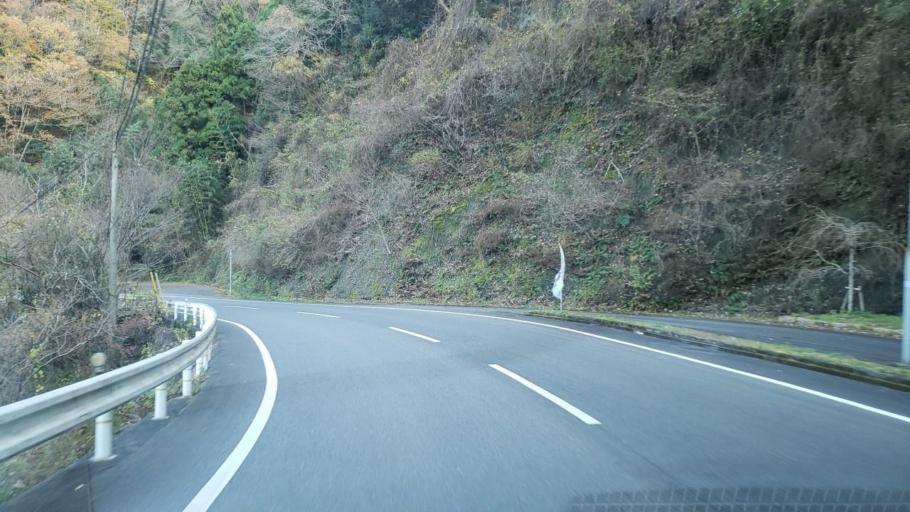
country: JP
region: Tokushima
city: Wakimachi
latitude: 34.1676
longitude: 134.0757
